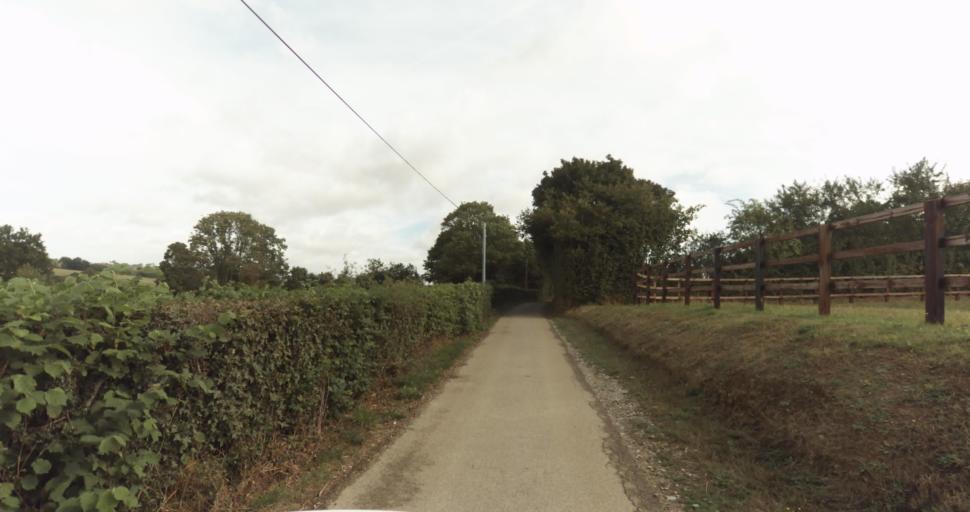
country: FR
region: Lower Normandy
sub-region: Departement de l'Orne
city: Gace
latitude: 48.8349
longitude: 0.3841
